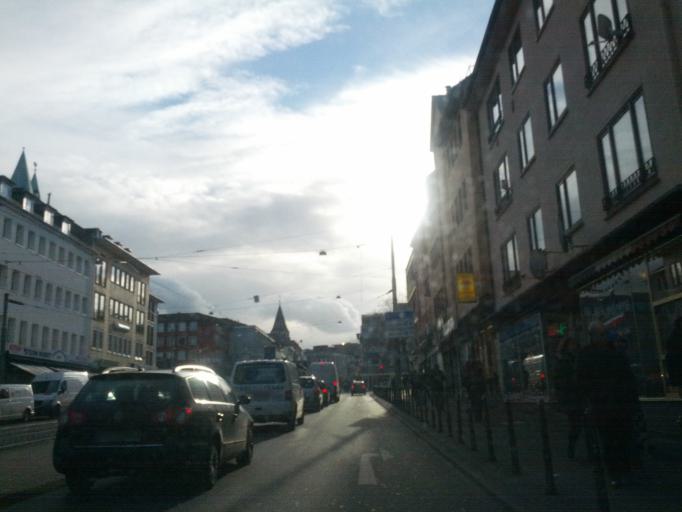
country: DE
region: Hesse
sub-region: Regierungsbezirk Kassel
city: Kassel
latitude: 51.3189
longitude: 9.5008
